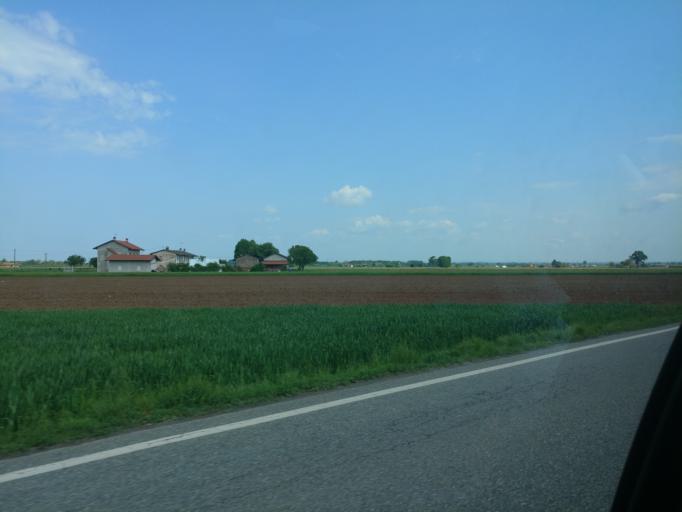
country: IT
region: Piedmont
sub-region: Provincia di Torino
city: Cavour
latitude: 44.7706
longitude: 7.3914
